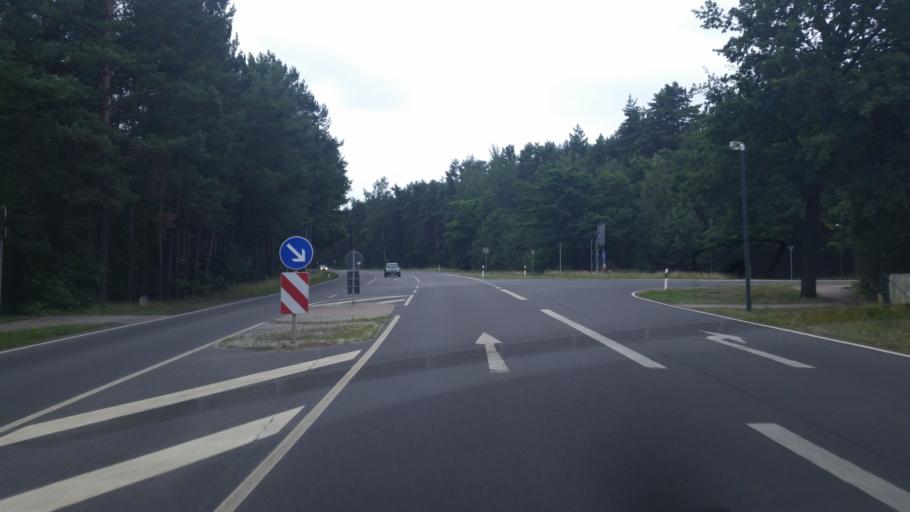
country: DE
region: Brandenburg
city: Senftenberg
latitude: 51.4880
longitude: 14.0678
